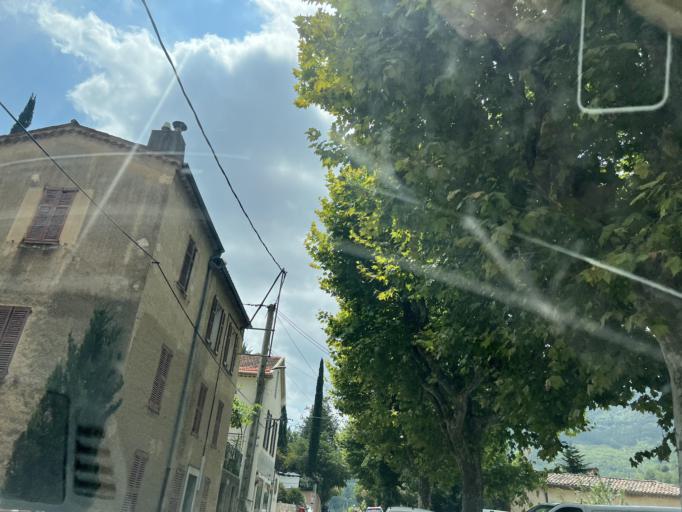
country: FR
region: Provence-Alpes-Cote d'Azur
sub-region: Departement des Alpes-Maritimes
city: Le Rouret
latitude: 43.7191
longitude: 6.9926
